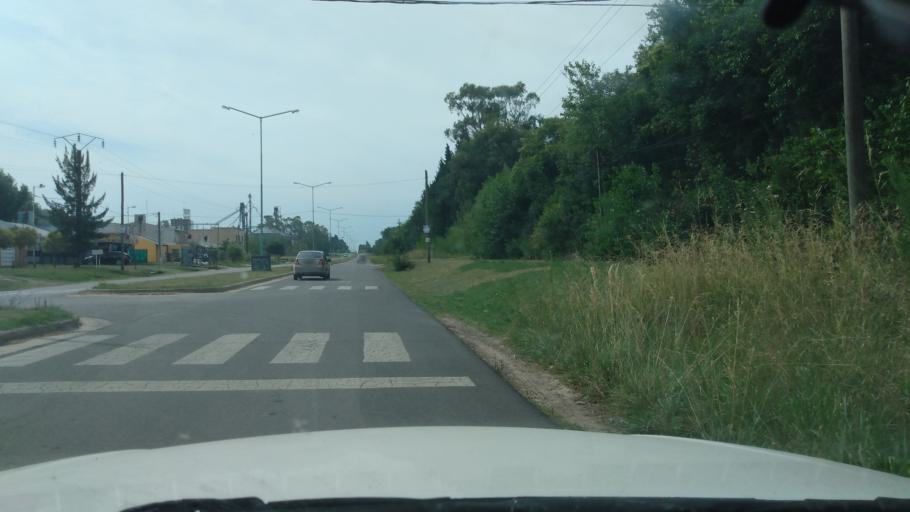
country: AR
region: Buenos Aires
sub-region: Partido de Lujan
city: Lujan
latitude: -34.5538
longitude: -59.1329
